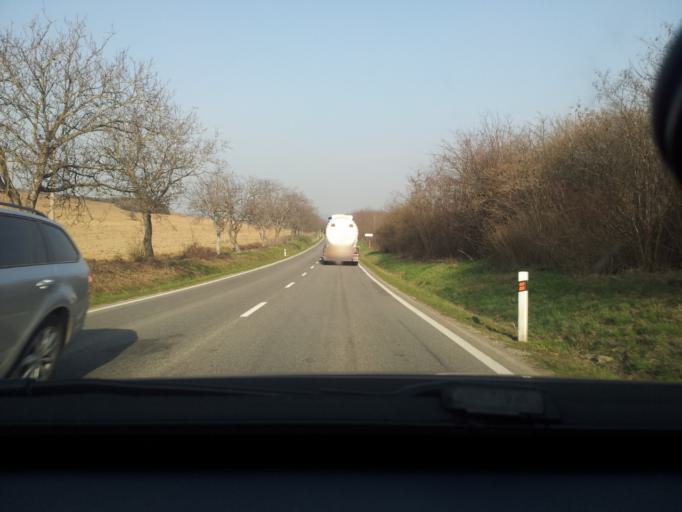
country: SK
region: Nitriansky
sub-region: Okres Nitra
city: Nitra
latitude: 48.3547
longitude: 17.9420
